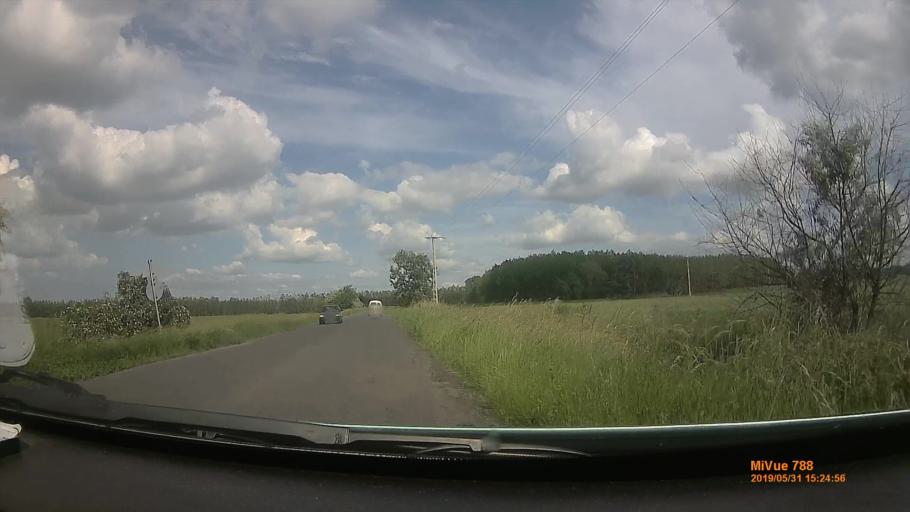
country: HU
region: Borsod-Abauj-Zemplen
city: Taktaharkany
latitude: 48.0663
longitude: 21.1610
